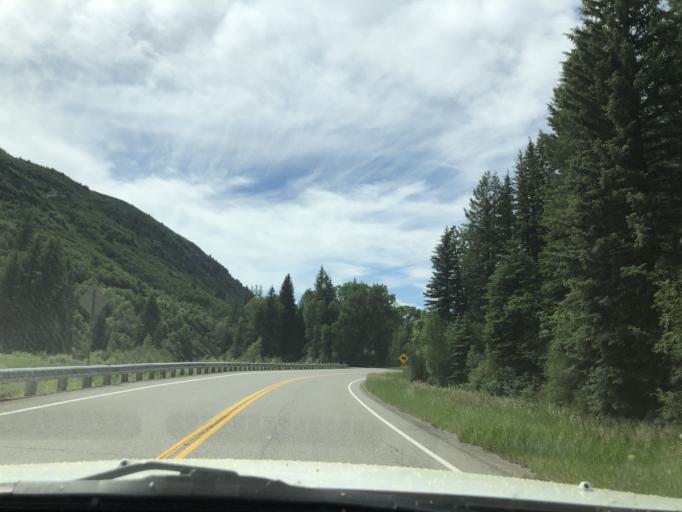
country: US
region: Colorado
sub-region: Delta County
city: Paonia
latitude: 38.9887
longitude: -107.3489
